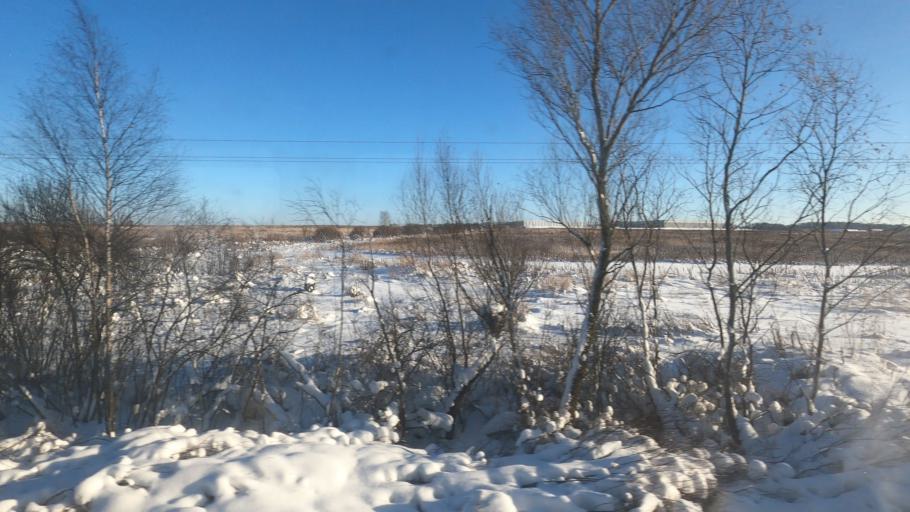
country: RU
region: Moskovskaya
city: Orud'yevo
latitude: 56.4225
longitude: 37.4978
